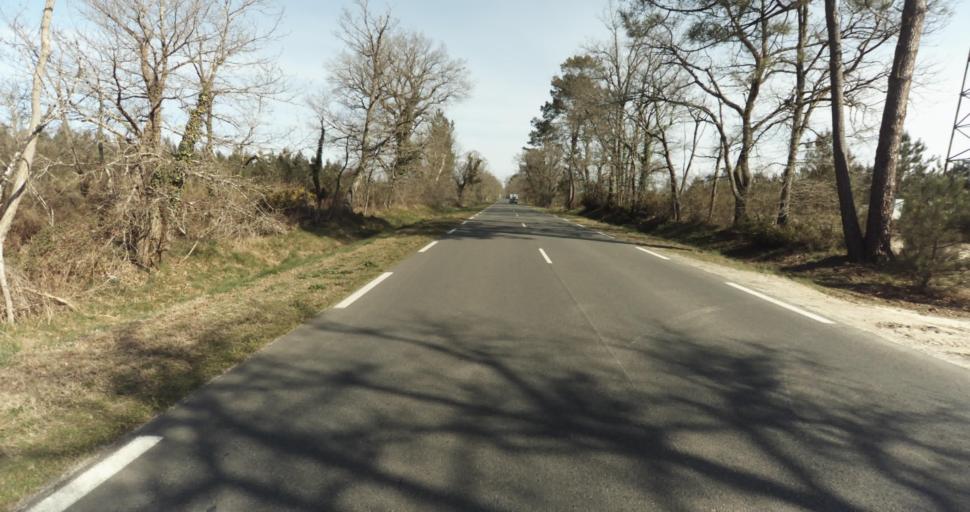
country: FR
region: Aquitaine
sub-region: Departement des Landes
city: Roquefort
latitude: 44.0749
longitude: -0.3135
